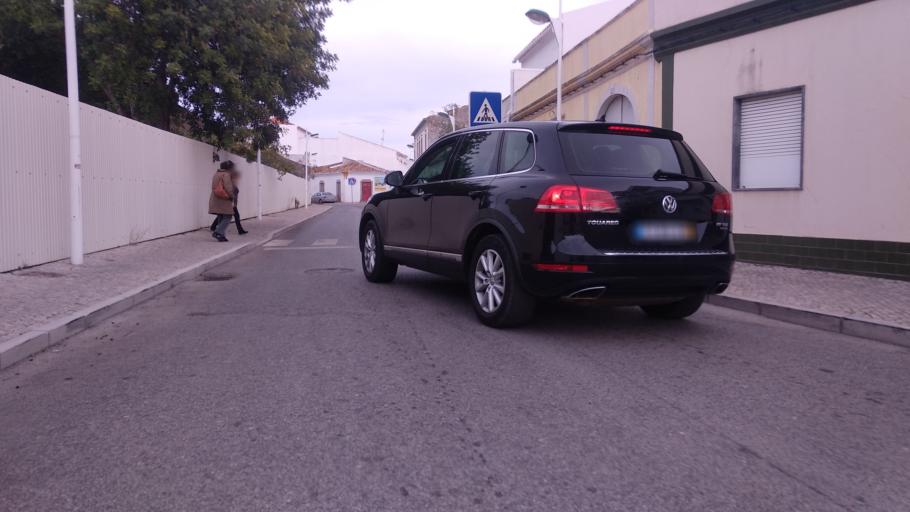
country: PT
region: Faro
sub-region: Sao Bras de Alportel
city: Sao Bras de Alportel
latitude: 37.1517
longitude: -7.8910
